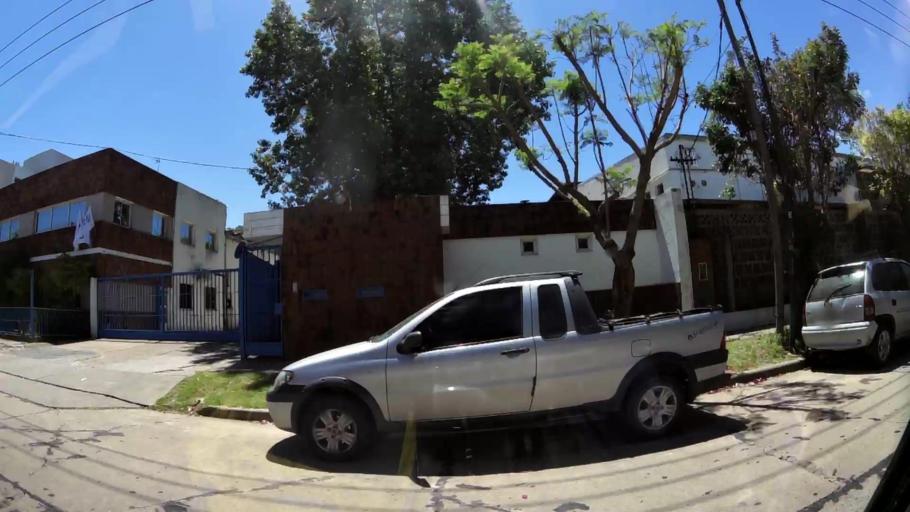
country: AR
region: Buenos Aires
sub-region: Partido de San Isidro
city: San Isidro
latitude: -34.5004
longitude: -58.5328
